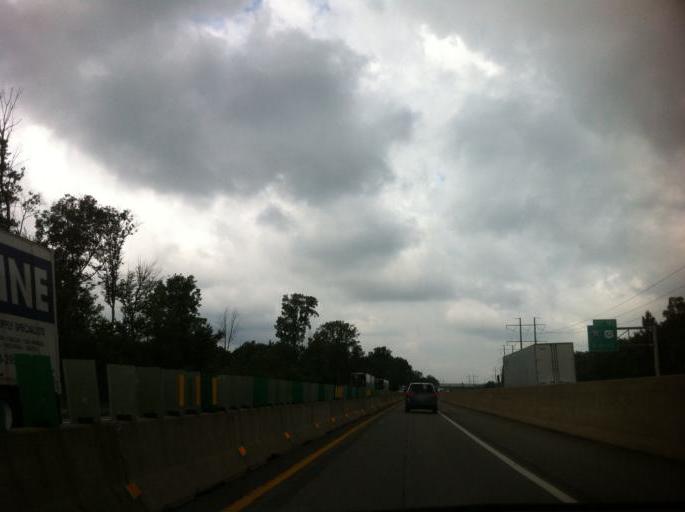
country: US
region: Ohio
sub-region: Cuyahoga County
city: Middleburg Heights
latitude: 41.3203
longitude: -81.7792
